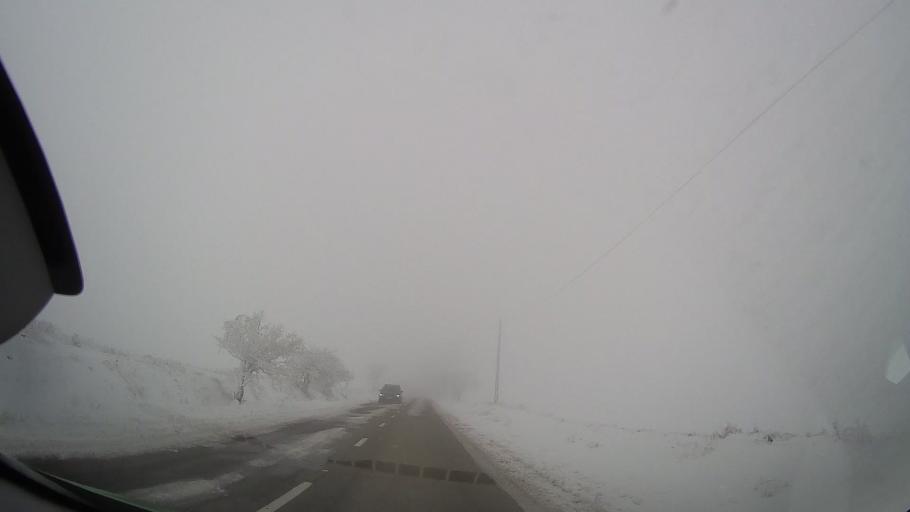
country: RO
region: Neamt
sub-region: Comuna Valea Ursului
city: Valea Ursului
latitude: 46.8039
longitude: 27.0724
